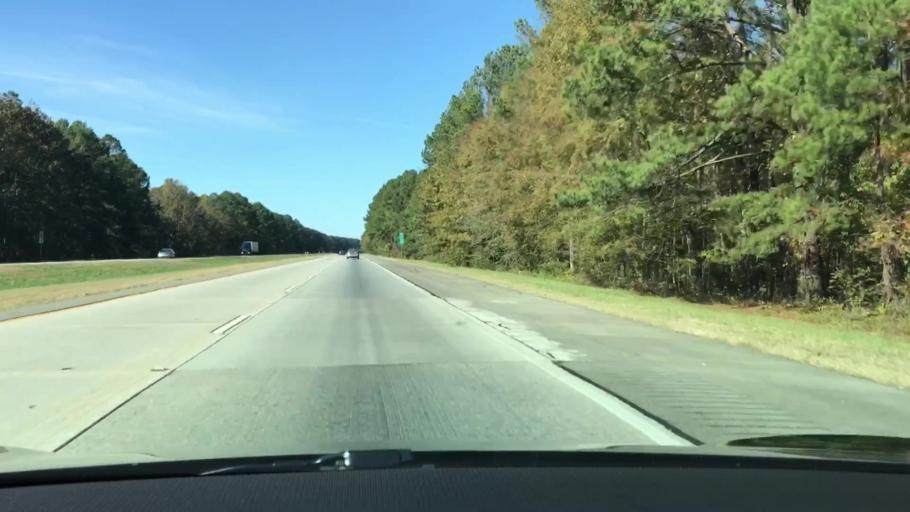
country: US
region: Georgia
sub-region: Taliaferro County
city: Crawfordville
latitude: 33.5302
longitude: -82.9731
